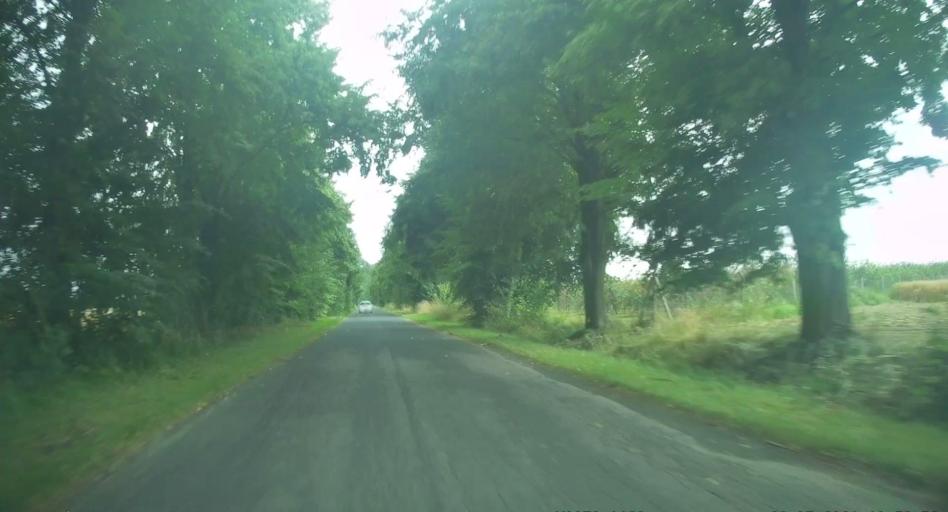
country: PL
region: Lodz Voivodeship
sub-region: Powiat rawski
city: Rawa Mazowiecka
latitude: 51.7662
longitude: 20.1839
